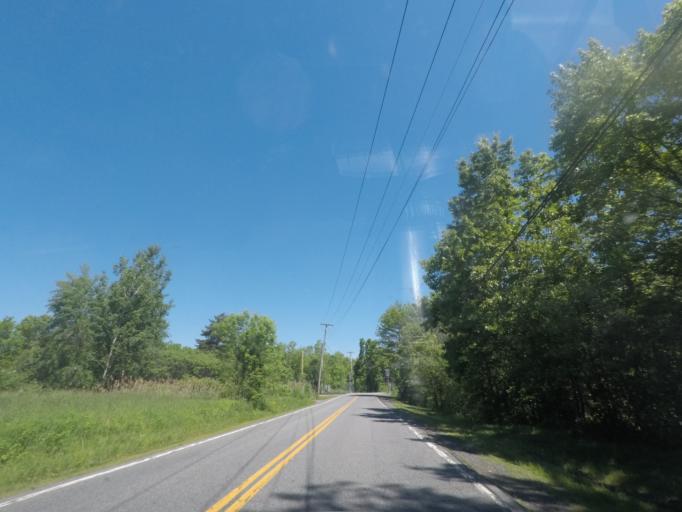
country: US
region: New York
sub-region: Schenectady County
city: East Glenville
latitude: 42.8850
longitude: -73.8647
